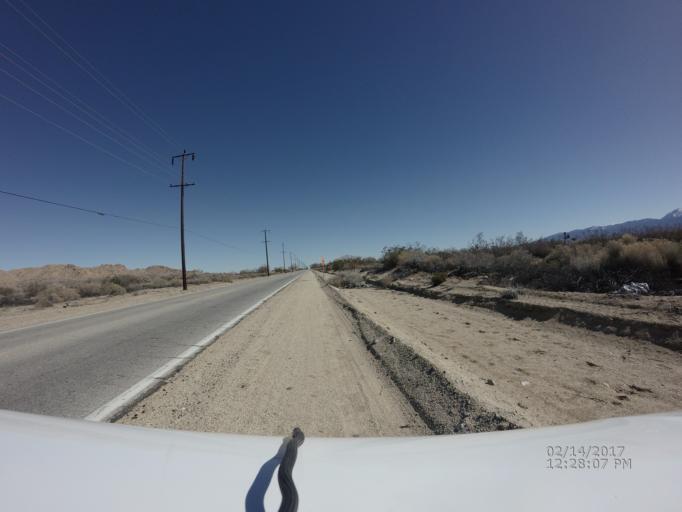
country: US
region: California
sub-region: Los Angeles County
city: Lake Los Angeles
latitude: 34.5800
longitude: -117.8794
